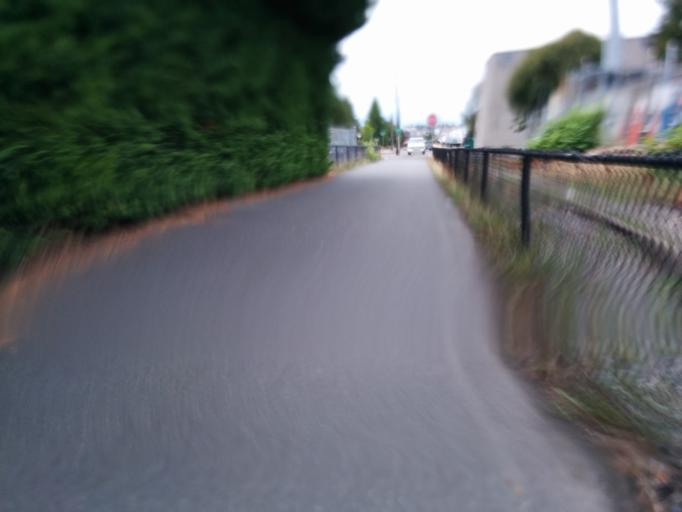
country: US
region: Washington
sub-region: King County
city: Seattle
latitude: 47.6585
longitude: -122.3654
